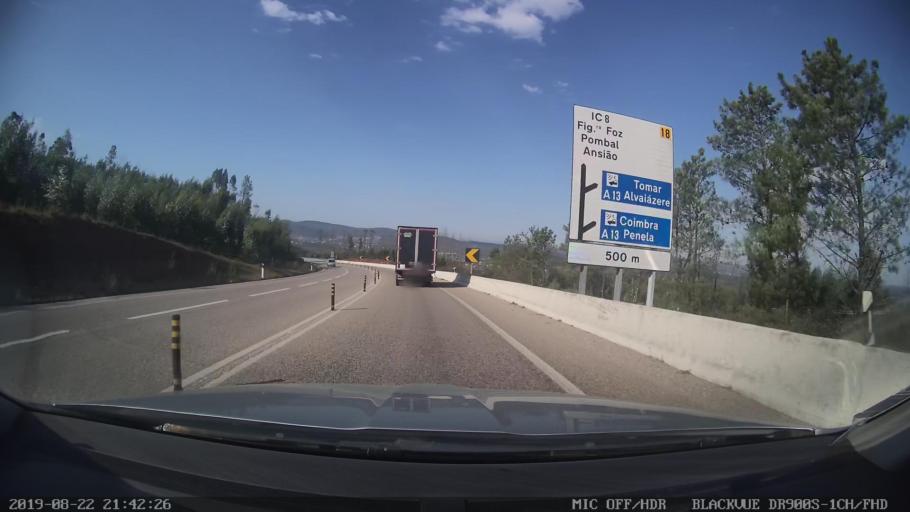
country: PT
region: Leiria
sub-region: Figueiro Dos Vinhos
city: Figueiro dos Vinhos
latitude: 39.9309
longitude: -8.3411
